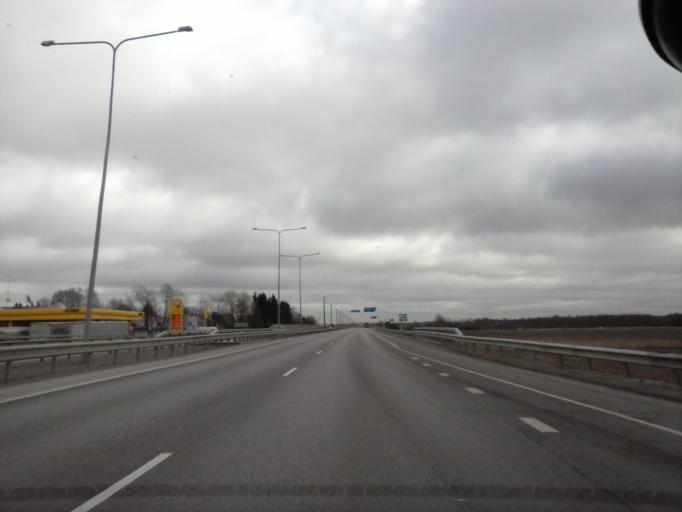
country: EE
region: Harju
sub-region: Rae vald
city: Jueri
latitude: 59.3598
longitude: 24.8721
